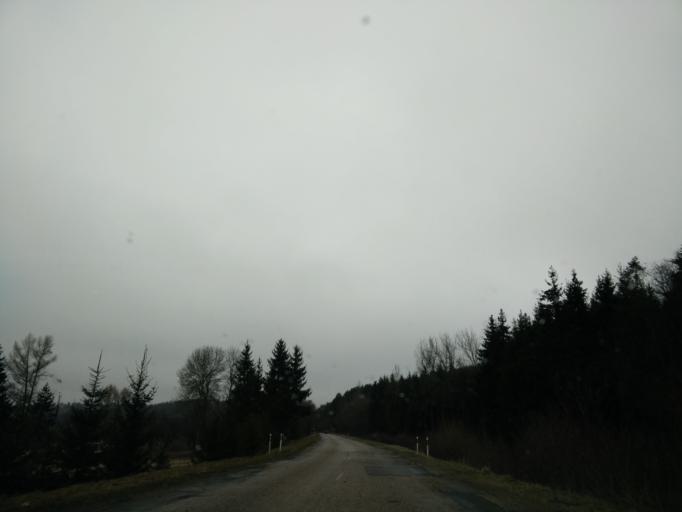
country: LT
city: Ariogala
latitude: 55.2923
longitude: 23.4429
